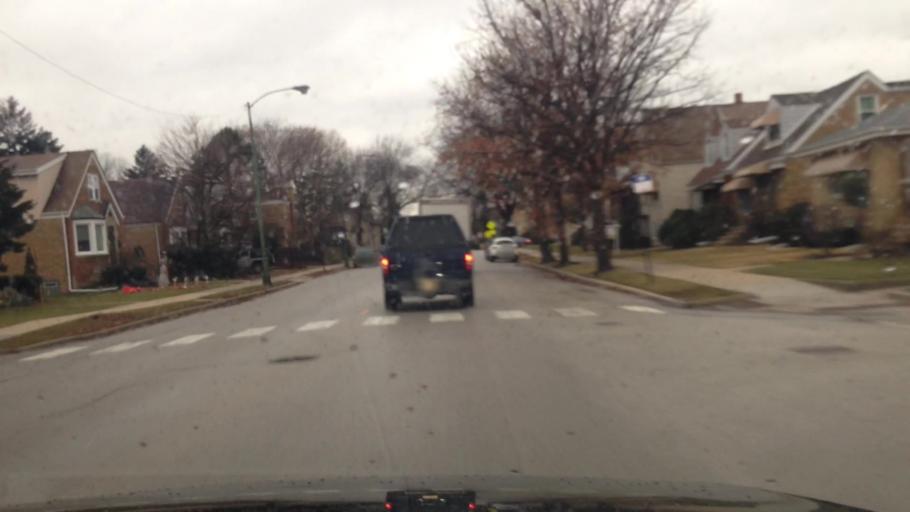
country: US
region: Illinois
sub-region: Cook County
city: Niles
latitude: 41.9974
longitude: -87.7908
